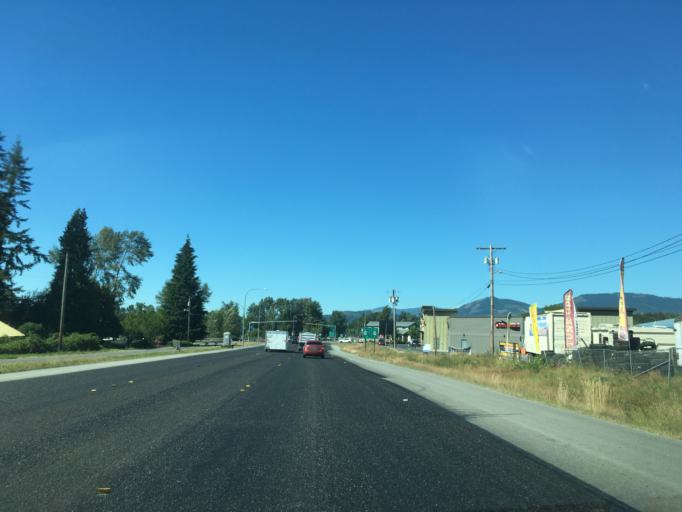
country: US
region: Washington
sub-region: Snohomish County
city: Arlington
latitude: 48.1970
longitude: -122.1290
